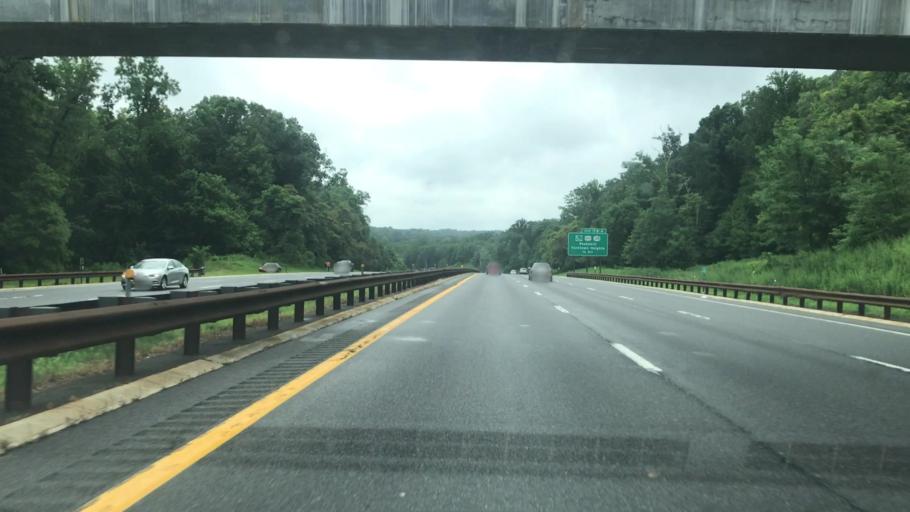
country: US
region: New York
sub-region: Westchester County
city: Shrub Oak
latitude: 41.3097
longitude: -73.8241
